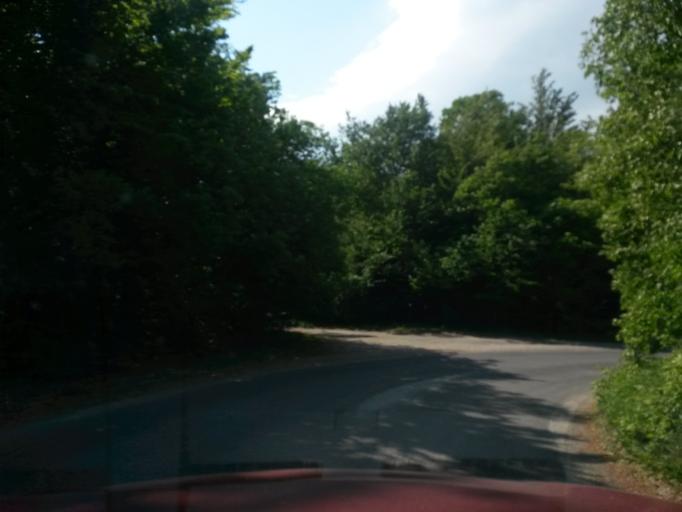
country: SK
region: Kosicky
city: Moldava nad Bodvou
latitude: 48.7221
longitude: 21.0384
